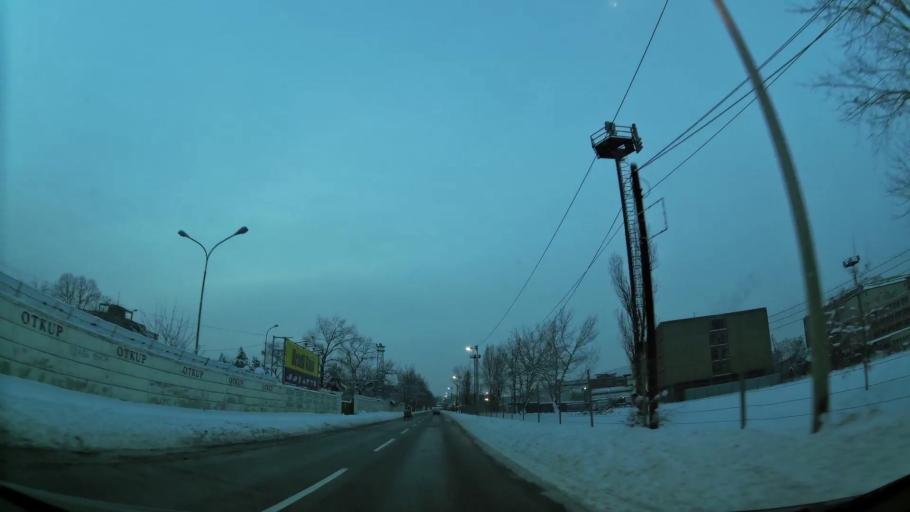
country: RS
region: Central Serbia
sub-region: Belgrade
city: Stari Grad
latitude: 44.8214
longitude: 20.4824
